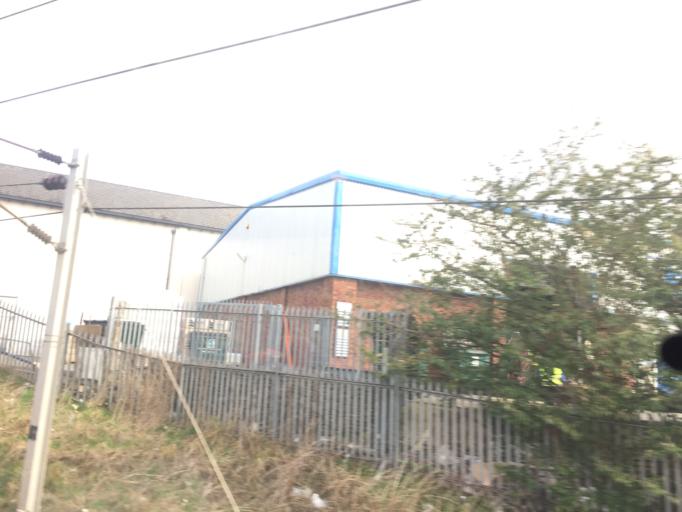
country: GB
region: England
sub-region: Cumbria
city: Penrith
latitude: 54.6641
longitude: -2.7585
